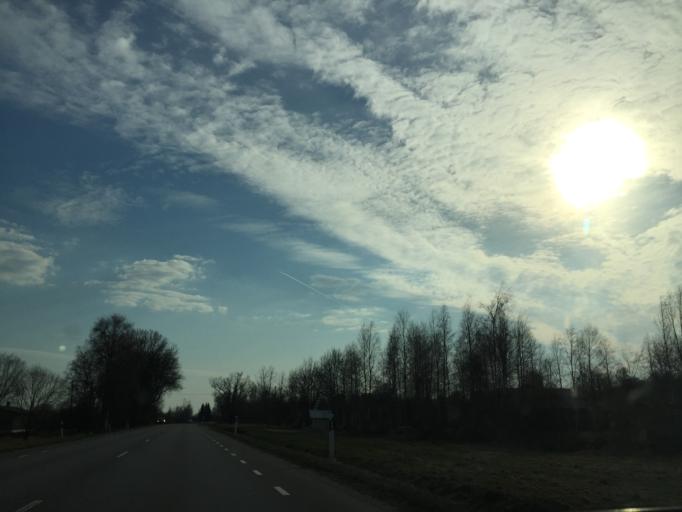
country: EE
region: Jogevamaa
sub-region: Mustvee linn
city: Mustvee
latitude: 58.9078
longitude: 27.0007
